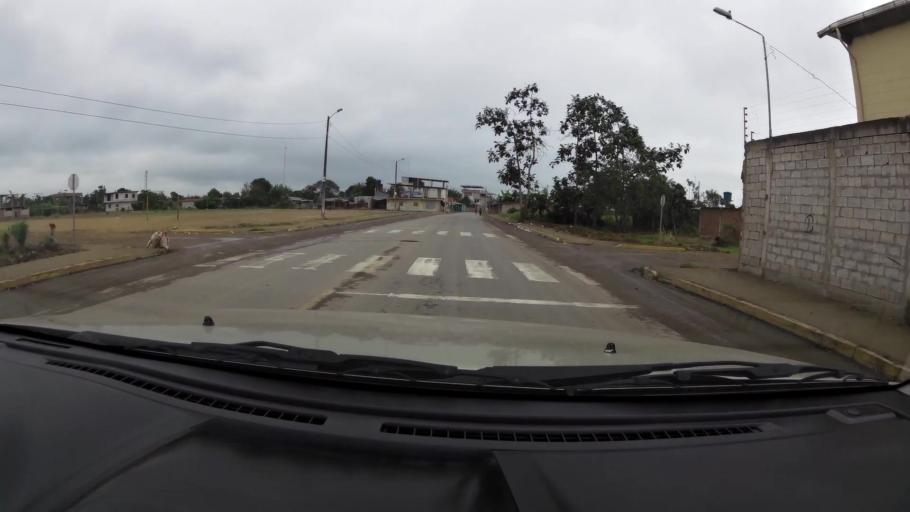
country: EC
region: El Oro
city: Pasaje
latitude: -3.3375
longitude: -79.8077
